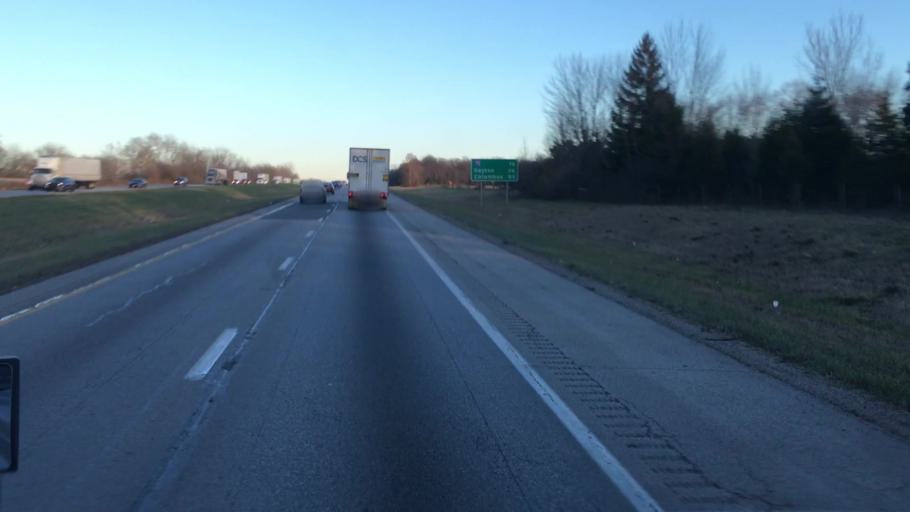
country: US
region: Ohio
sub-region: Preble County
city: Lewisburg
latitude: 39.8373
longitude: -84.5230
